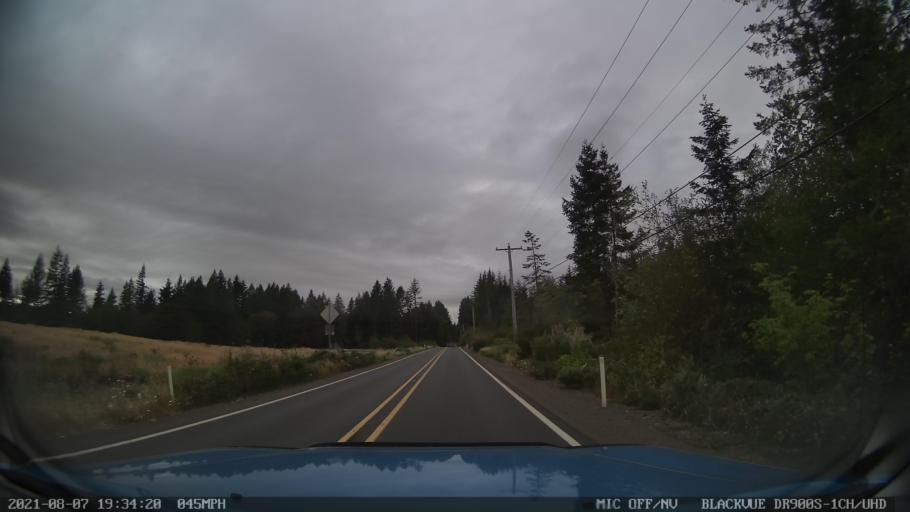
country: US
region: Oregon
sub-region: Linn County
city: Lyons
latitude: 44.9164
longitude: -122.6550
